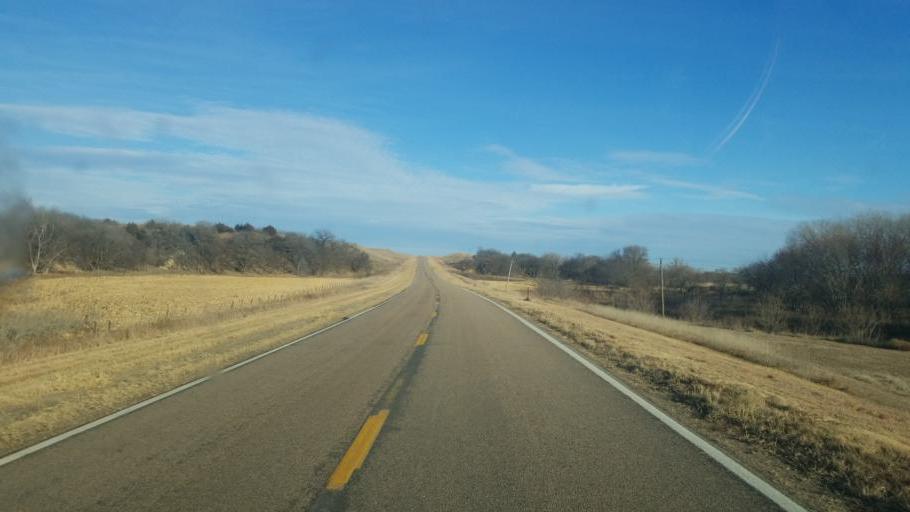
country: US
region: South Dakota
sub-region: Charles Mix County
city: Wagner
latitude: 42.8138
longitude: -98.2263
